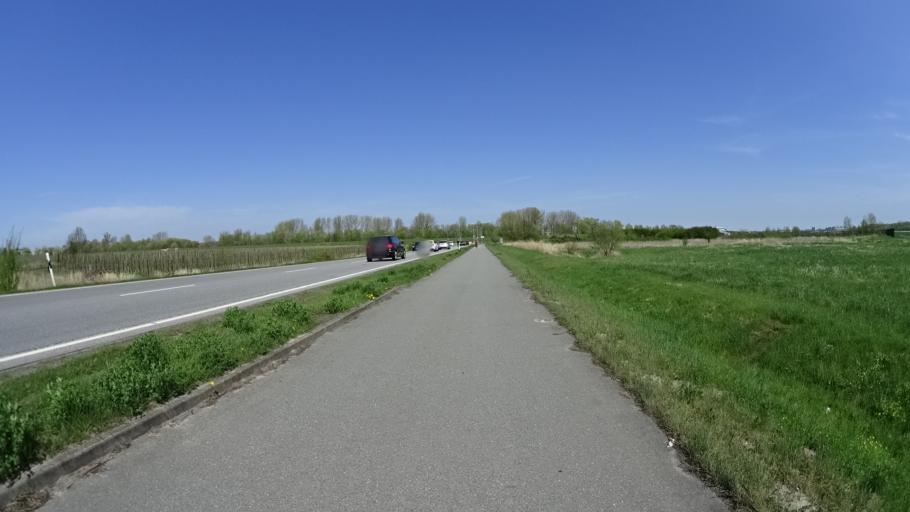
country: DE
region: Lower Saxony
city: Neu Wulmstorf
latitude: 53.5257
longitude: 9.8099
